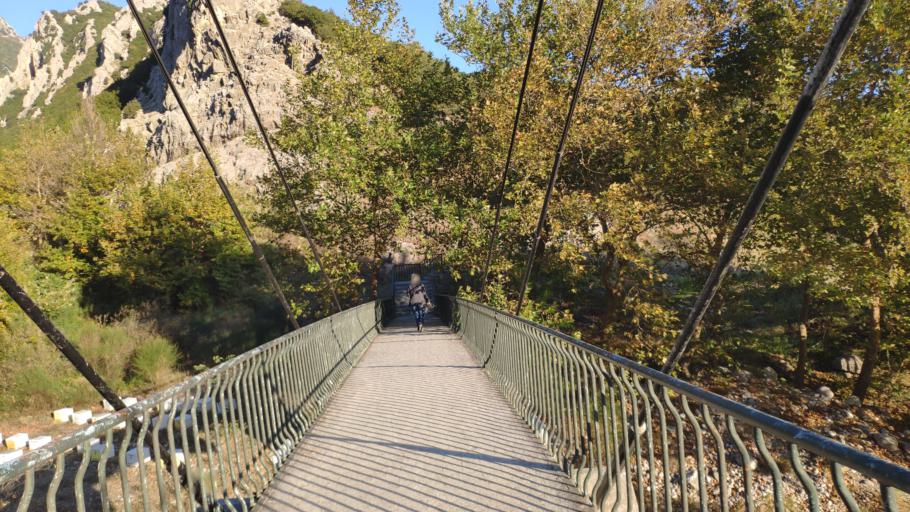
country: GR
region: Thessaly
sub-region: Trikala
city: Pyli
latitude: 39.4594
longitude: 21.6129
